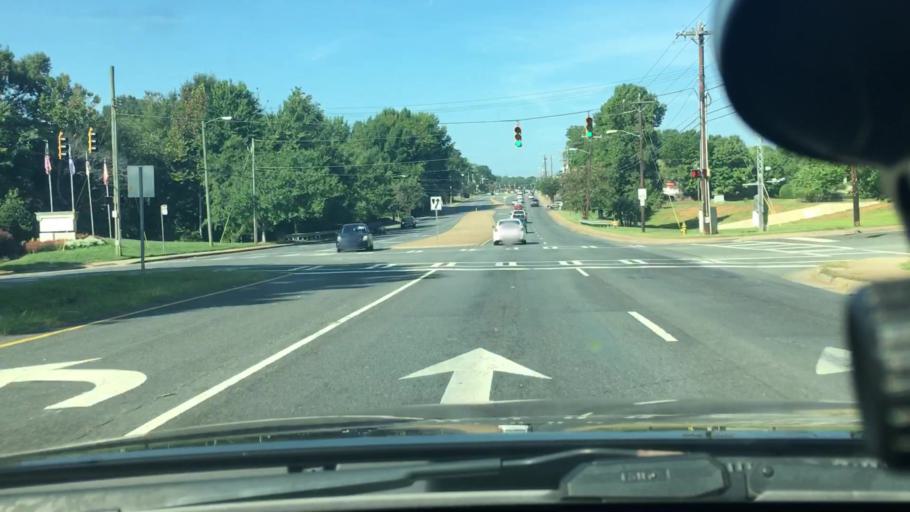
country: US
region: North Carolina
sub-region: Mecklenburg County
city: Mint Hill
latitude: 35.2052
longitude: -80.7179
